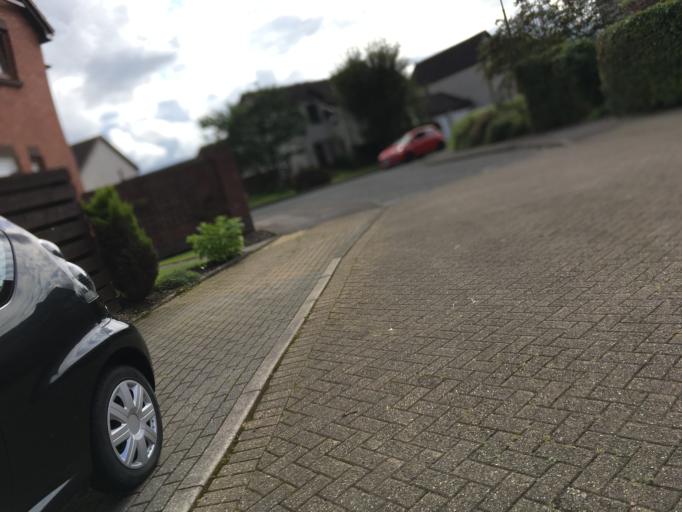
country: GB
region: Scotland
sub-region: West Lothian
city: Livingston
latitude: 55.8745
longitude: -3.5070
